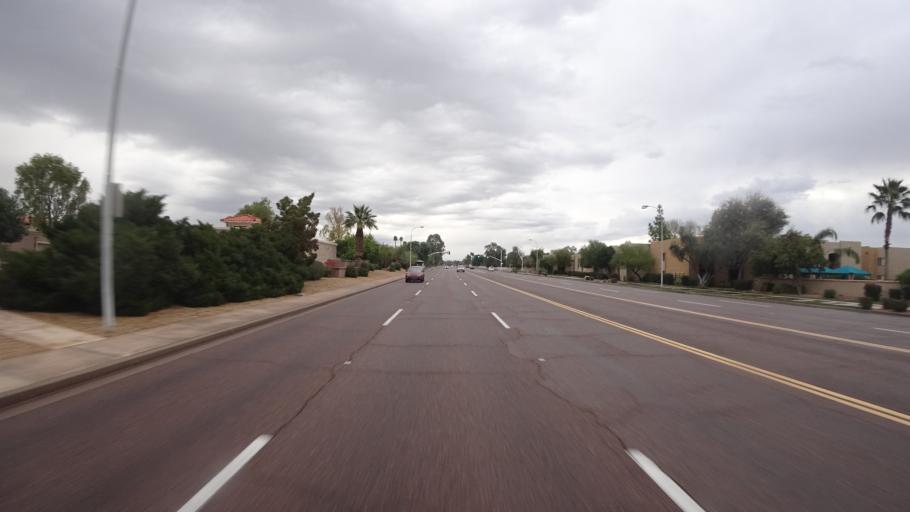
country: US
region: Arizona
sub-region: Maricopa County
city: Scottsdale
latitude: 33.5306
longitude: -111.9088
